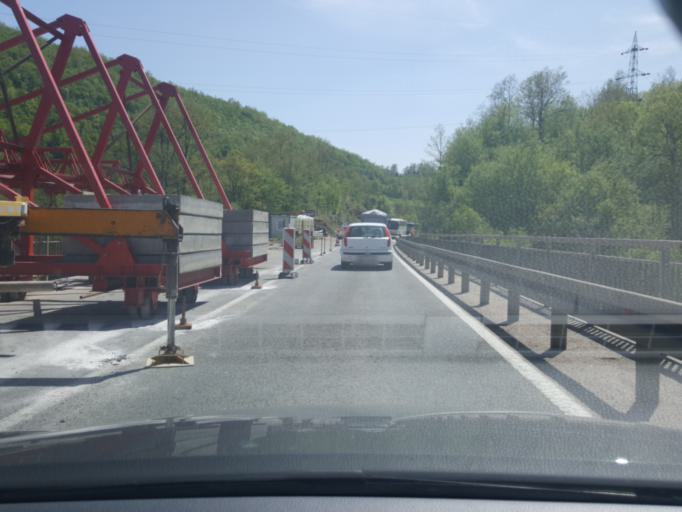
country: RS
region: Central Serbia
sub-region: Zlatiborski Okrug
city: Cajetina
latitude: 43.7863
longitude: 19.7532
